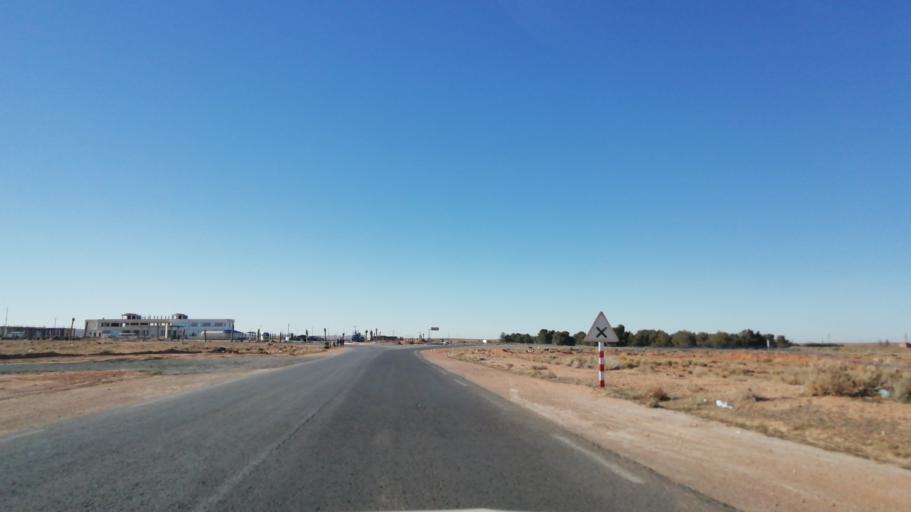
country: DZ
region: El Bayadh
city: El Bayadh
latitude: 33.6579
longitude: 0.9084
